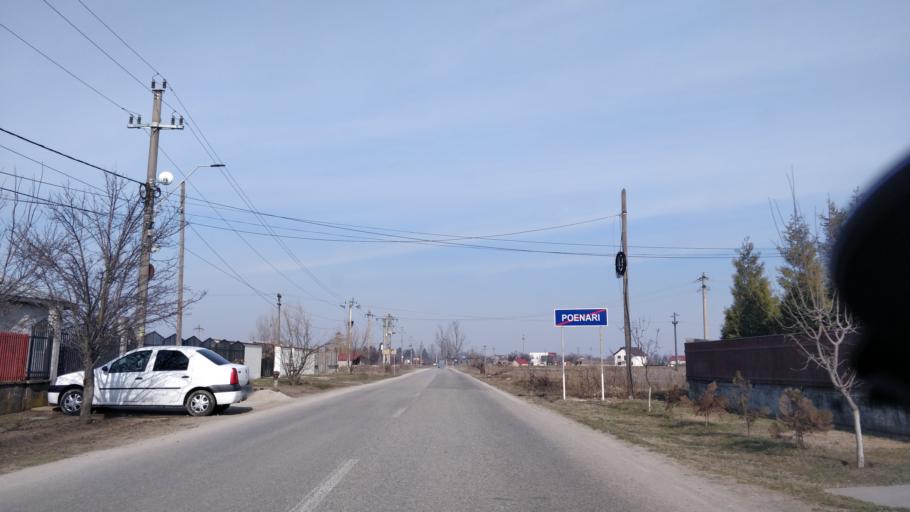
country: RO
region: Giurgiu
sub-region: Comuna Ulmi
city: Ulmi
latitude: 44.4796
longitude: 25.7703
